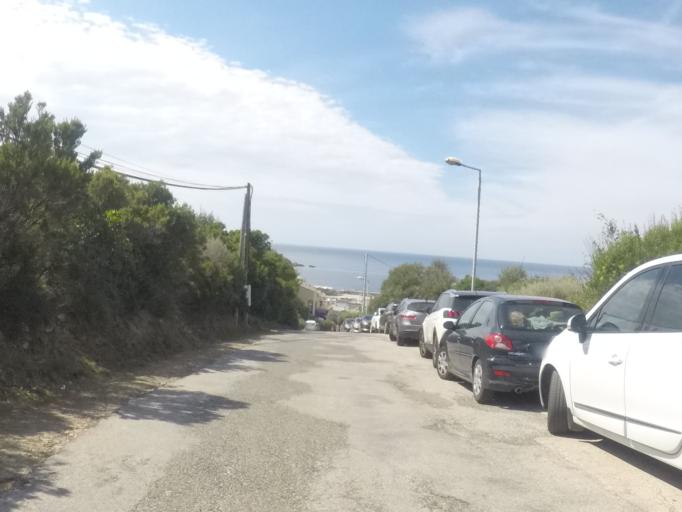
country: FR
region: Corsica
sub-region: Departement de la Haute-Corse
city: Brando
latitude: 42.9659
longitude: 9.3548
